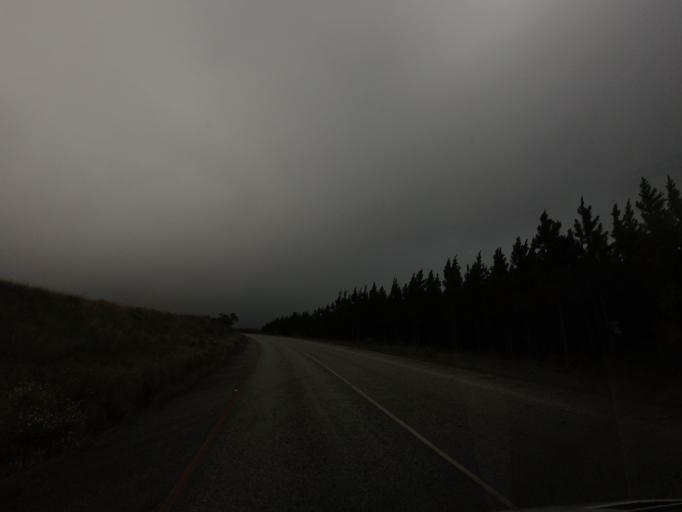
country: ZA
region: Mpumalanga
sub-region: Ehlanzeni District
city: Graksop
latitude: -24.8619
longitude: 30.8912
